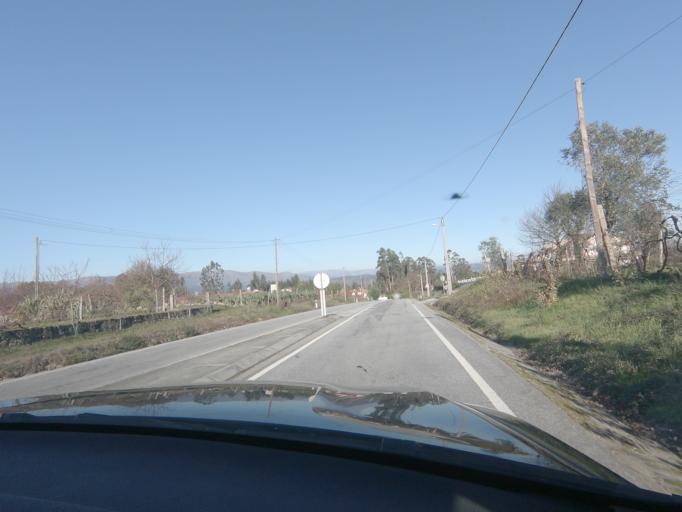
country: PT
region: Viseu
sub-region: Vouzela
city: Vouzela
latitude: 40.7175
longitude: -8.1339
